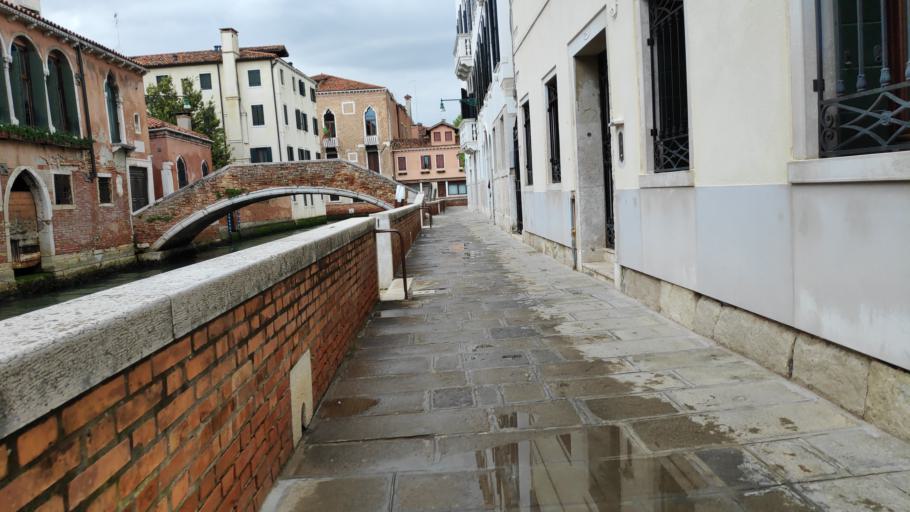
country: IT
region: Veneto
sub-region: Provincia di Venezia
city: Giudecca
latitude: 45.4325
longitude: 12.3202
